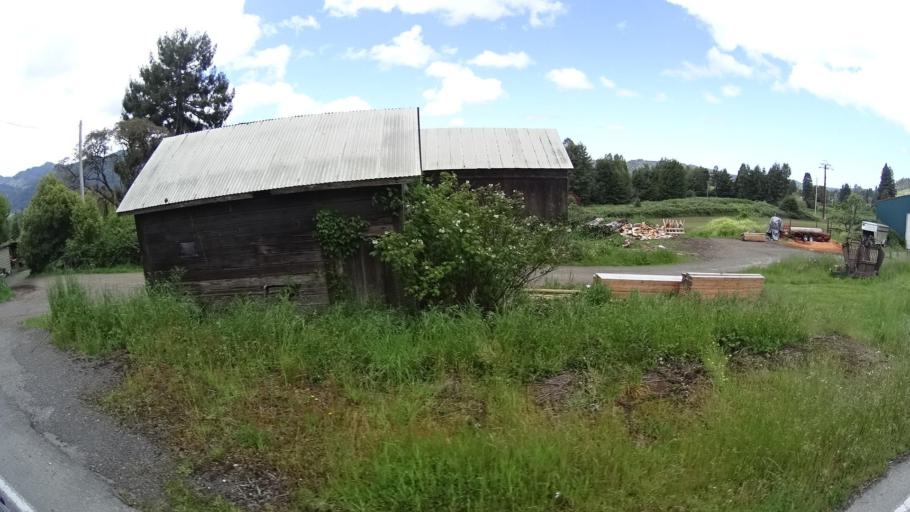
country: US
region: California
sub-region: Humboldt County
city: Blue Lake
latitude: 40.8764
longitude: -123.9797
